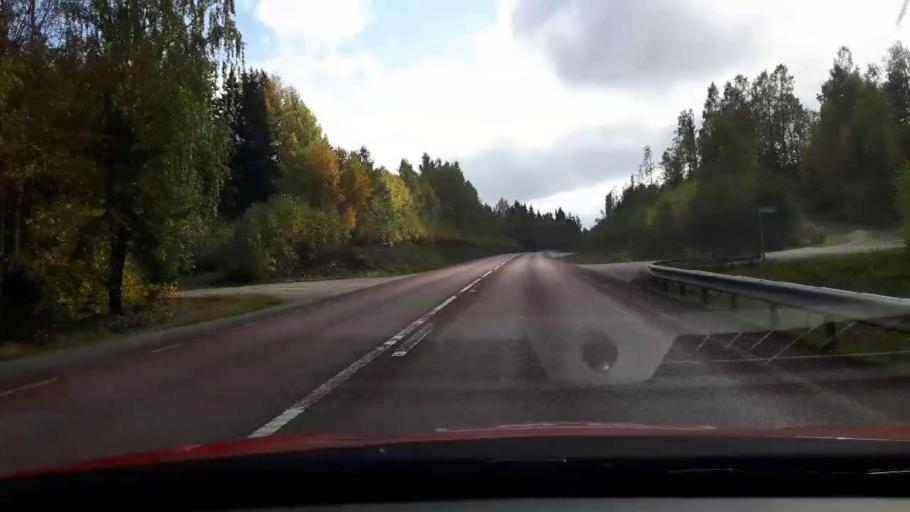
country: SE
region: Gaevleborg
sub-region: Ljusdals Kommun
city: Jaervsoe
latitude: 61.6206
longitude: 16.2891
